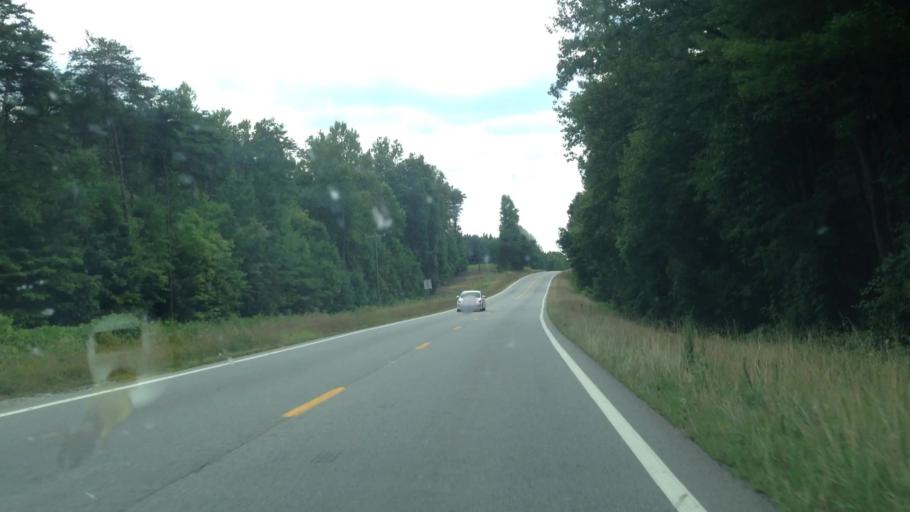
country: US
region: North Carolina
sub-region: Guilford County
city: Stokesdale
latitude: 36.2717
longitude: -79.9458
